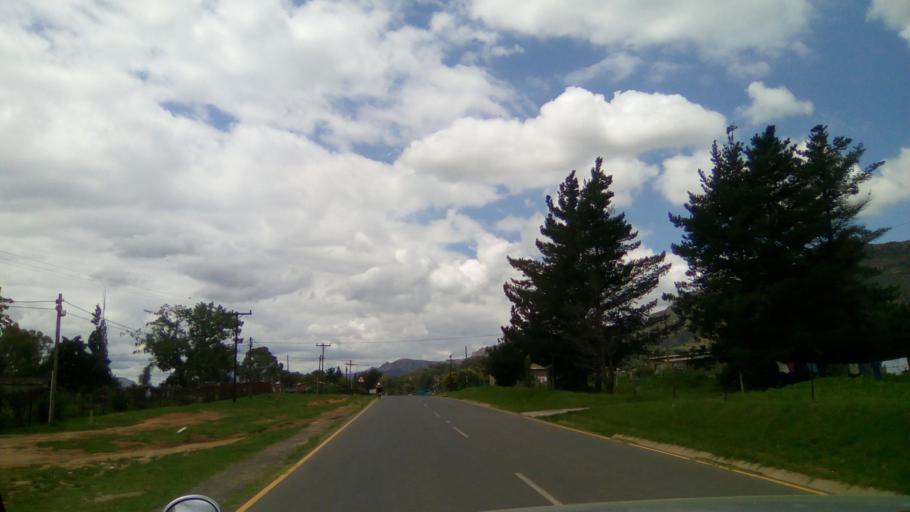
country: LS
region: Maseru
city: Nako
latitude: -29.6234
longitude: 27.5008
